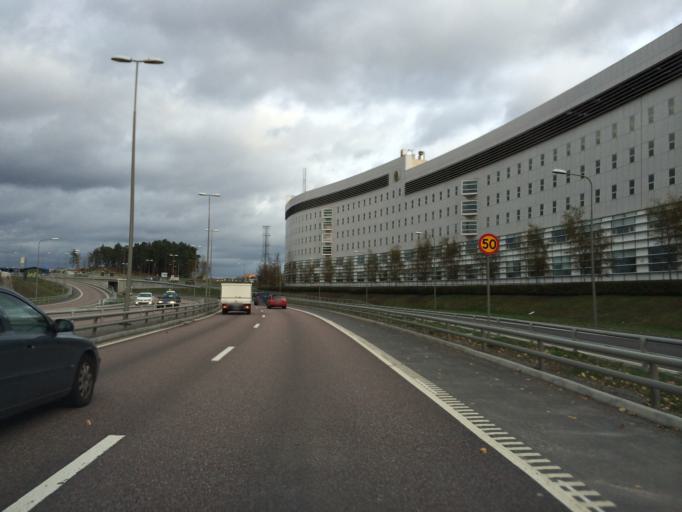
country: SE
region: Stockholm
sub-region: Stockholms Kommun
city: Kista
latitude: 59.3799
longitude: 17.9332
